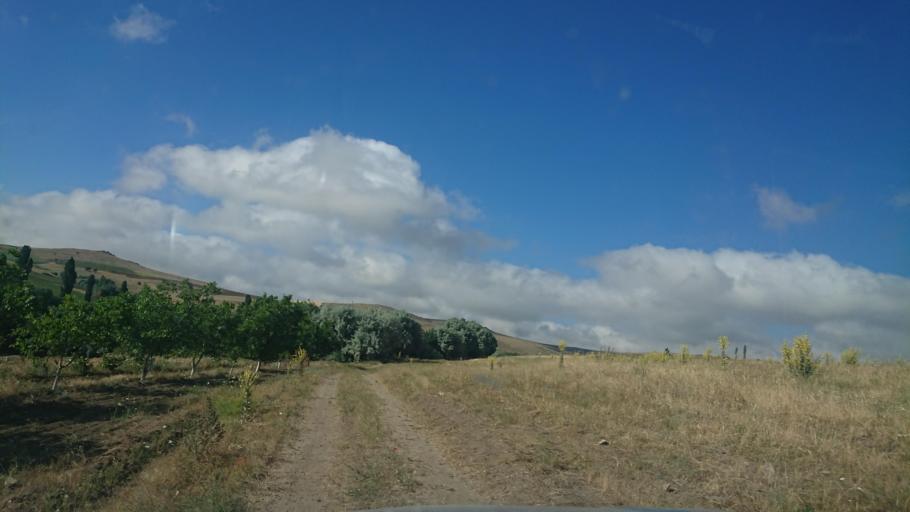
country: TR
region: Aksaray
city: Agacoren
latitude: 38.8500
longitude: 33.9293
